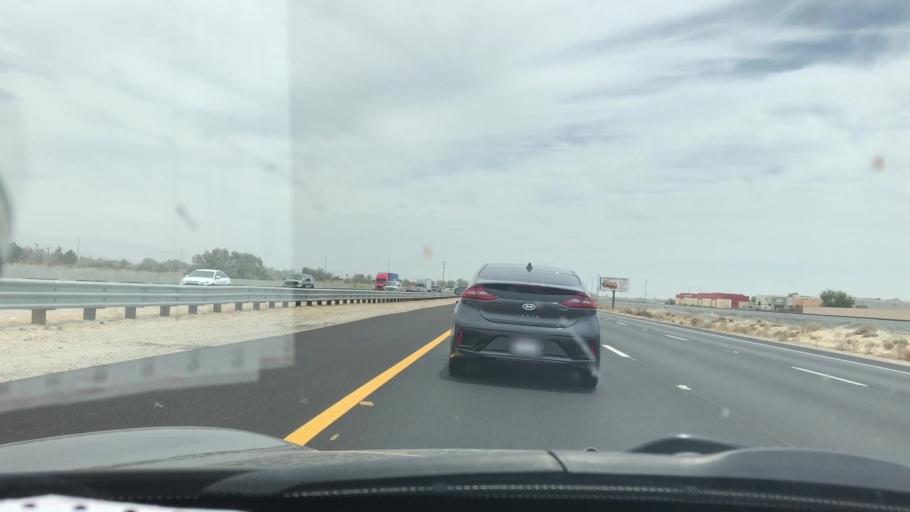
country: US
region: California
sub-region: Riverside County
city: Thousand Palms
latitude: 33.7995
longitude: -116.3776
